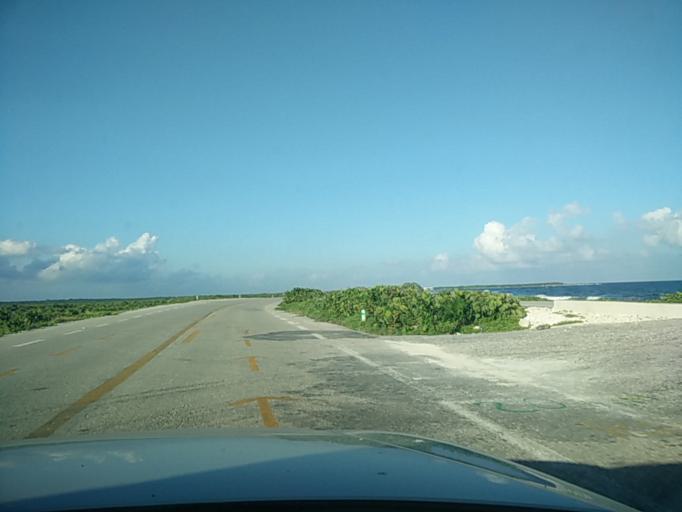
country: MX
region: Quintana Roo
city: San Miguel de Cozumel
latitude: 20.3365
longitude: -86.9153
